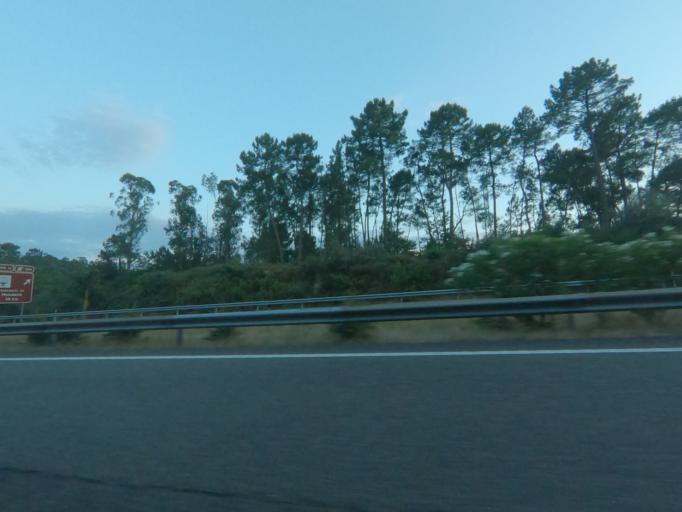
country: ES
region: Galicia
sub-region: Provincia de Pontevedra
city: Ponteareas
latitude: 42.1561
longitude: -8.5198
